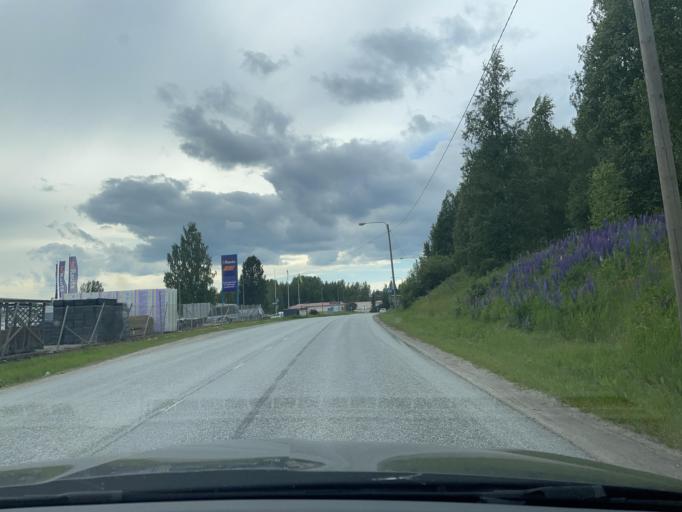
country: FI
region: Central Finland
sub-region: Jaemsae
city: Jaemsae
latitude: 61.8574
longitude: 25.1840
